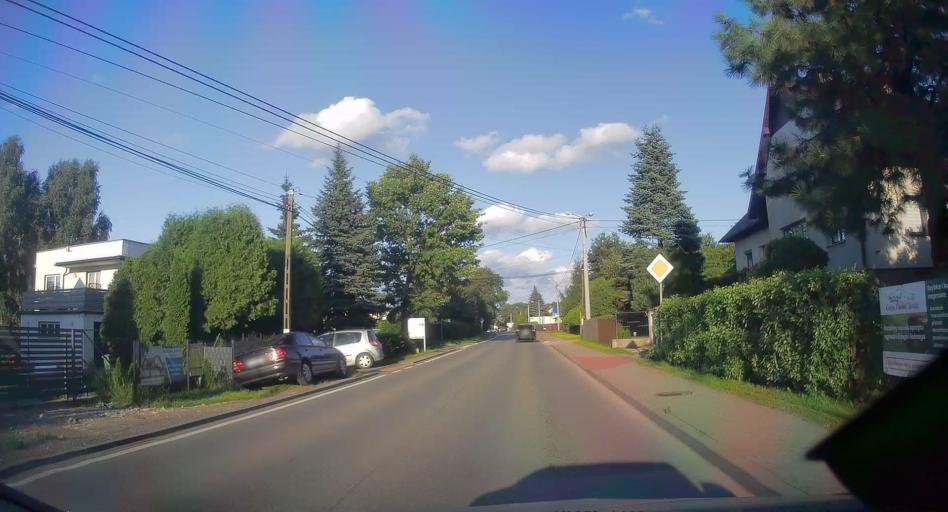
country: PL
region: Lesser Poland Voivodeship
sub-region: Powiat wielicki
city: Kokotow
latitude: 50.0122
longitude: 20.0787
